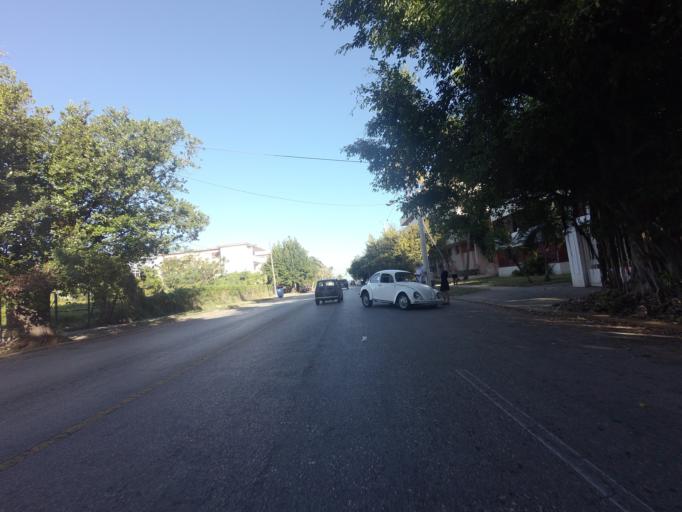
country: CU
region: La Habana
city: Havana
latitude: 23.1201
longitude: -82.4252
